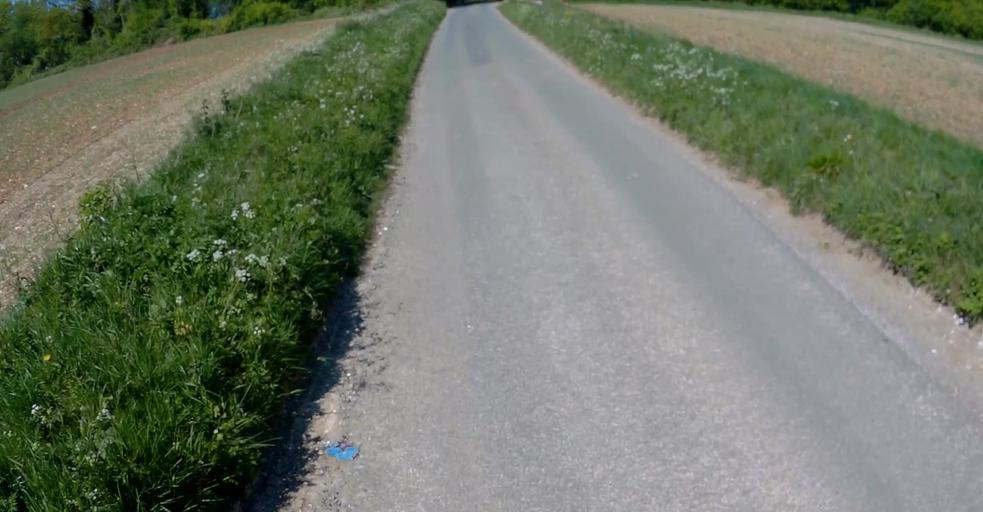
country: GB
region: England
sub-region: Hampshire
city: Overton
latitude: 51.2135
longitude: -1.3105
